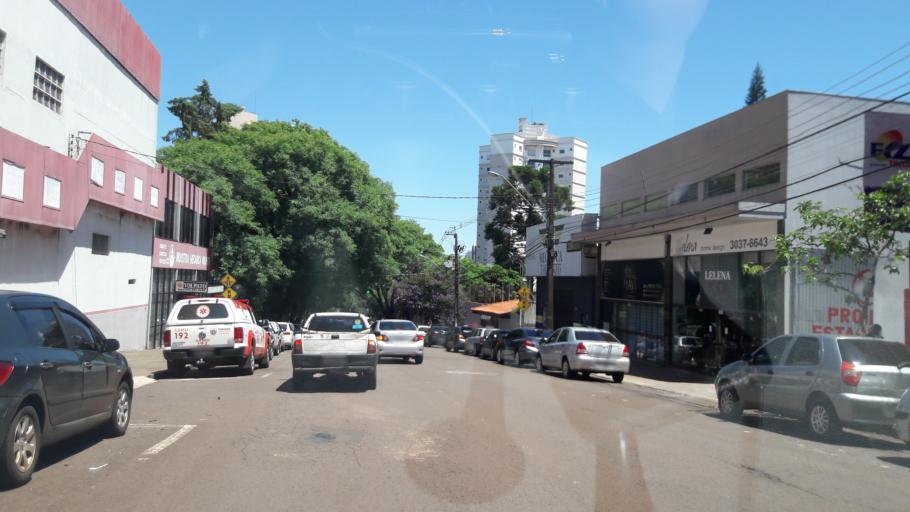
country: BR
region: Parana
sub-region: Cascavel
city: Cascavel
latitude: -24.9495
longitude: -53.4446
